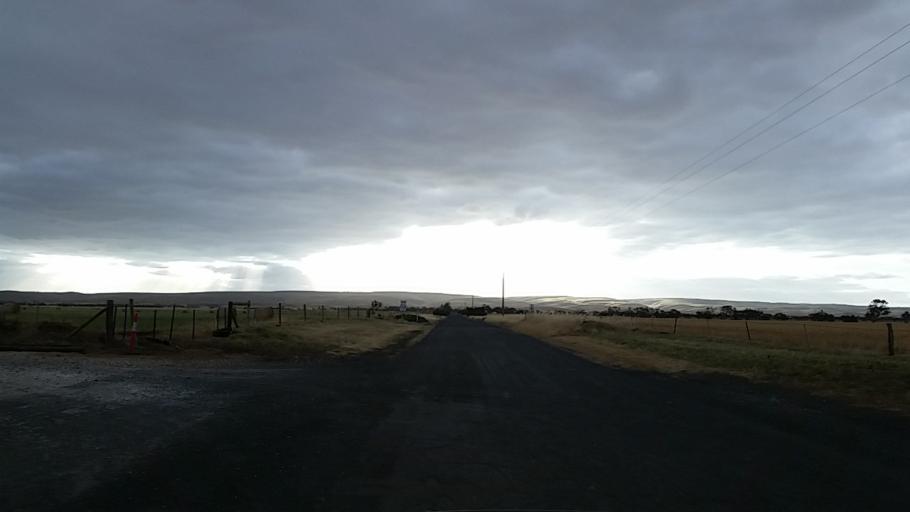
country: AU
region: South Australia
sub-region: Barossa
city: Angaston
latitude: -34.5729
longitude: 139.2919
